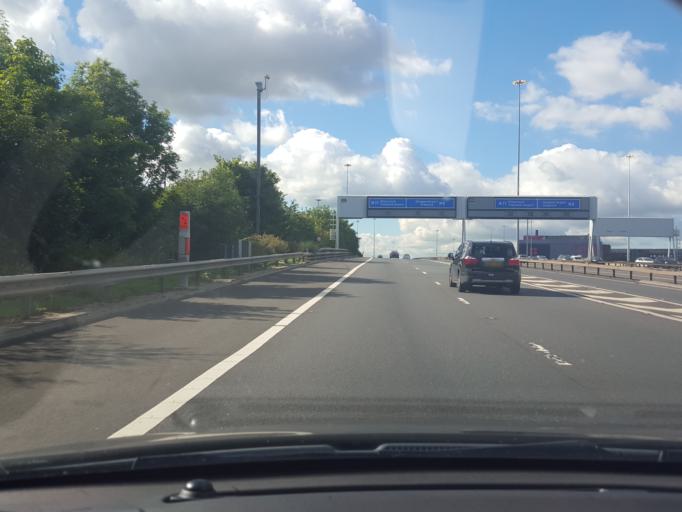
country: GB
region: Scotland
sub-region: Glasgow City
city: Glasgow
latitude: 55.8506
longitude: -4.2737
